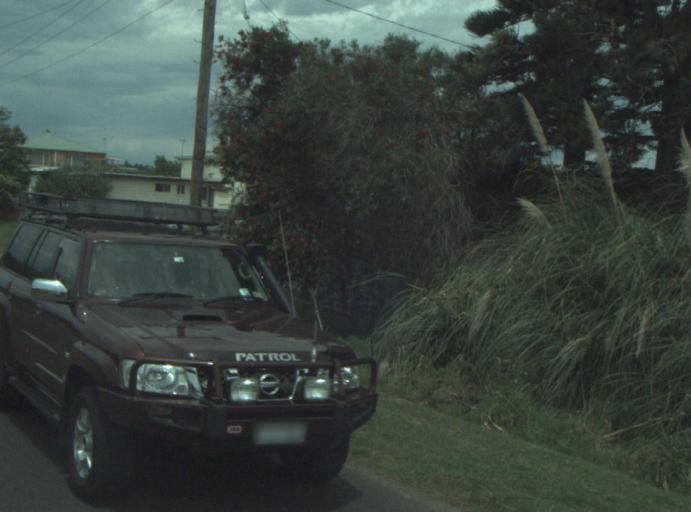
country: AU
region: Victoria
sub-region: Greater Geelong
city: Clifton Springs
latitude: -38.1125
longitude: 144.6294
